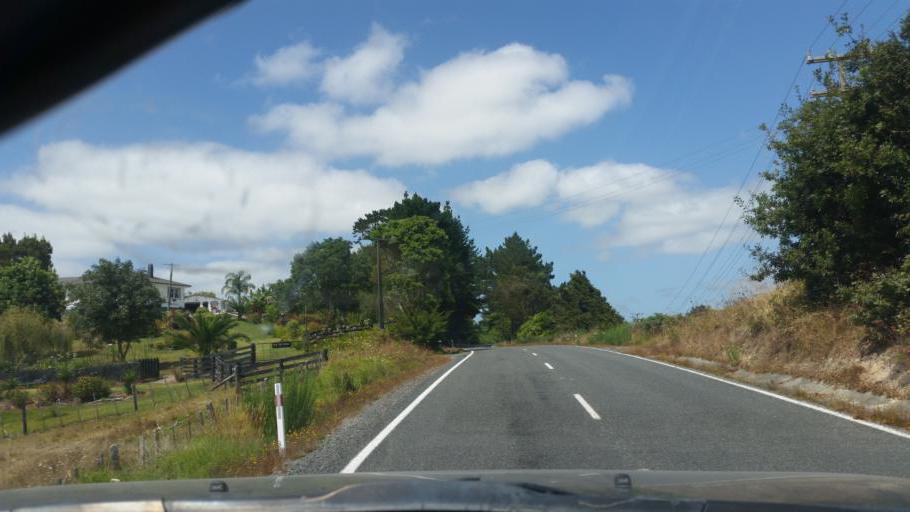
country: NZ
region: Northland
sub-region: Whangarei
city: Ruakaka
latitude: -36.0675
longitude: 174.2655
